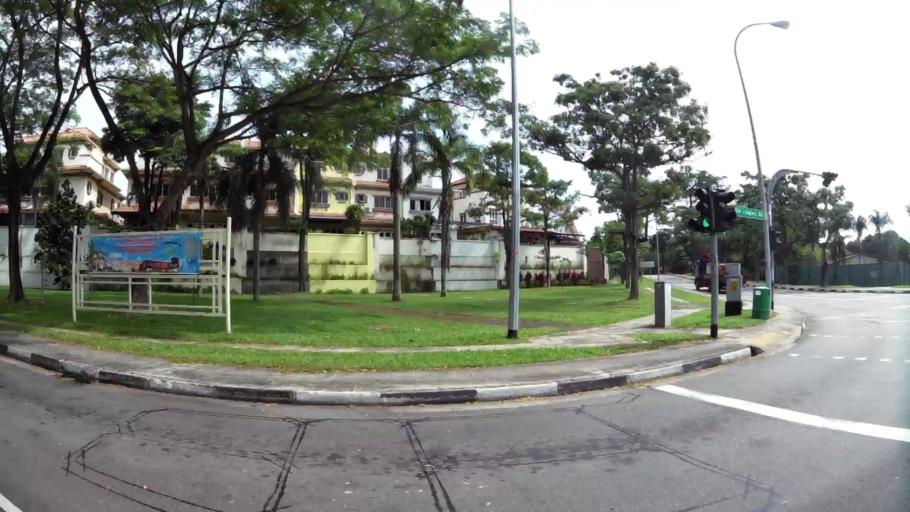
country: SG
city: Singapore
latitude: 1.3619
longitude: 103.9717
